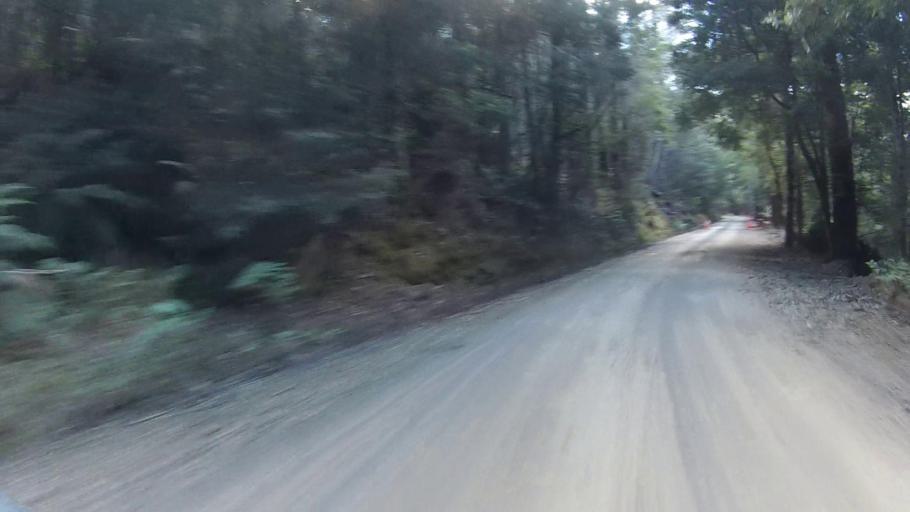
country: AU
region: Tasmania
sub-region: Derwent Valley
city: New Norfolk
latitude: -42.6806
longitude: 146.6820
